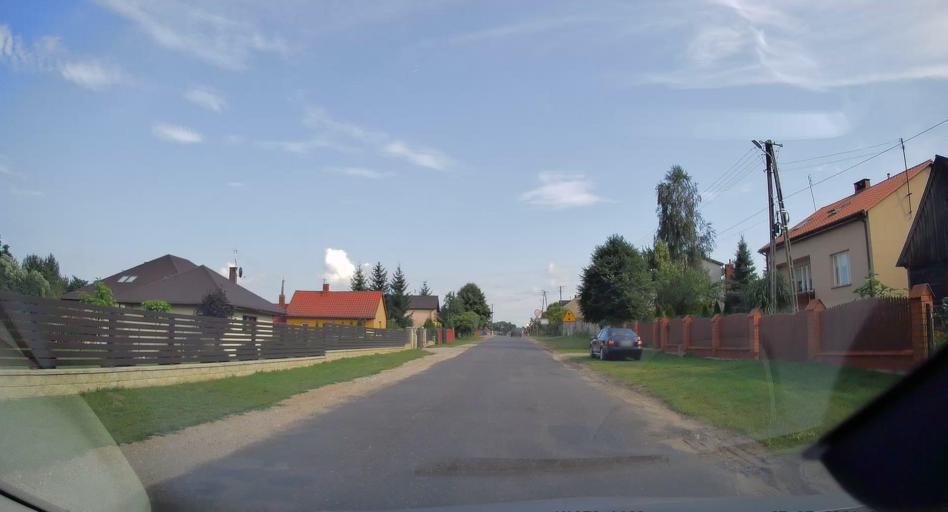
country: PL
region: Lodz Voivodeship
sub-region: Powiat opoczynski
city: Bialaczow
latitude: 51.3225
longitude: 20.3498
